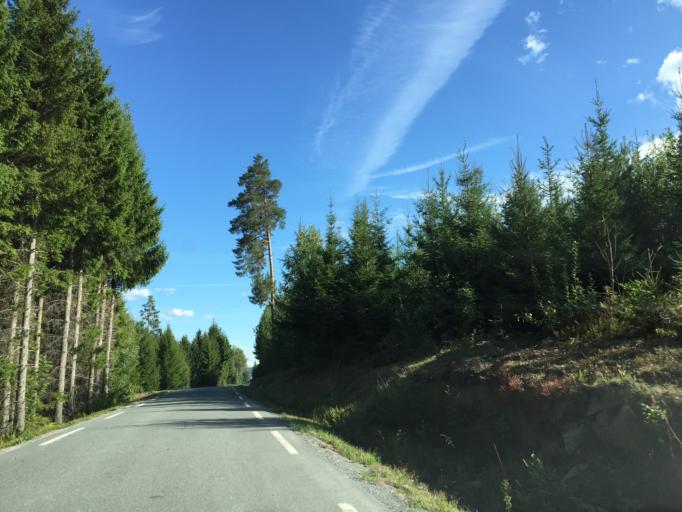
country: NO
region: Buskerud
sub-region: Ovre Eiker
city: Hokksund
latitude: 59.6593
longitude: 9.9038
